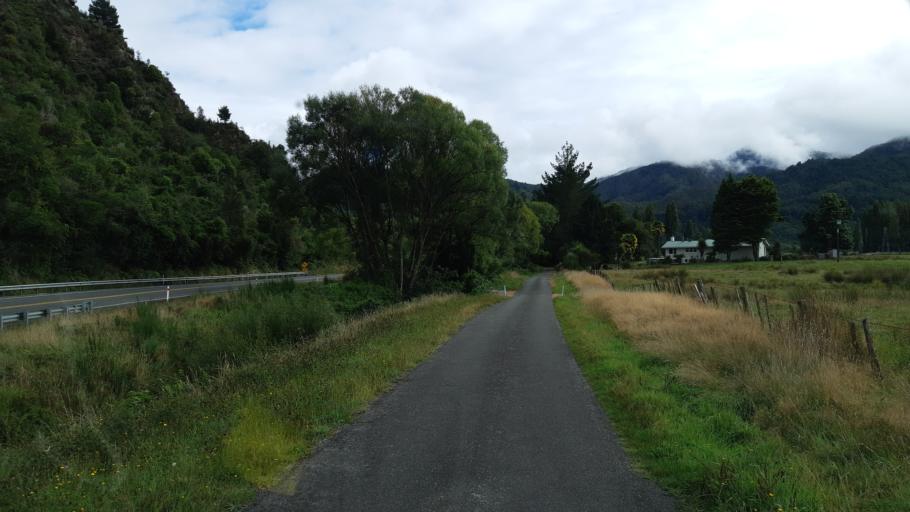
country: NZ
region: West Coast
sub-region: Buller District
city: Westport
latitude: -41.7839
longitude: 172.2762
